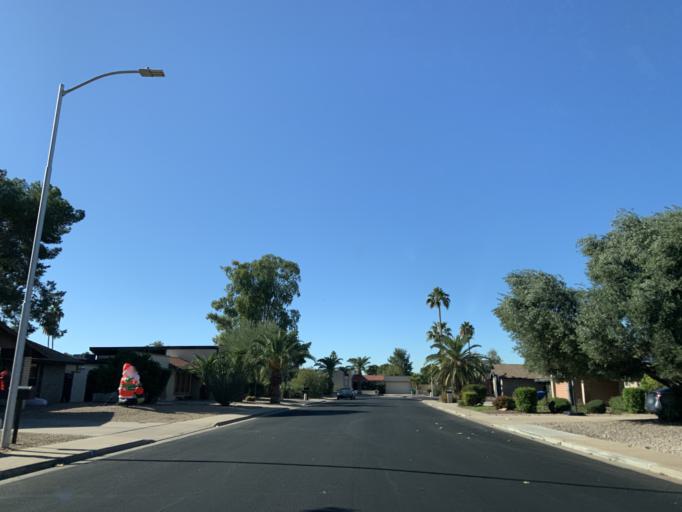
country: US
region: Arizona
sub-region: Maricopa County
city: San Carlos
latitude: 33.3607
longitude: -111.8621
